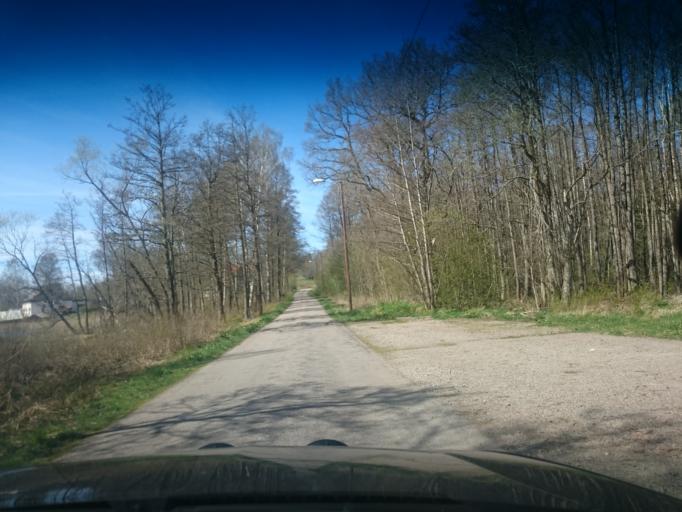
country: SE
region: Kalmar
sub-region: Hultsfreds Kommun
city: Virserum
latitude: 57.3666
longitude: 15.3957
